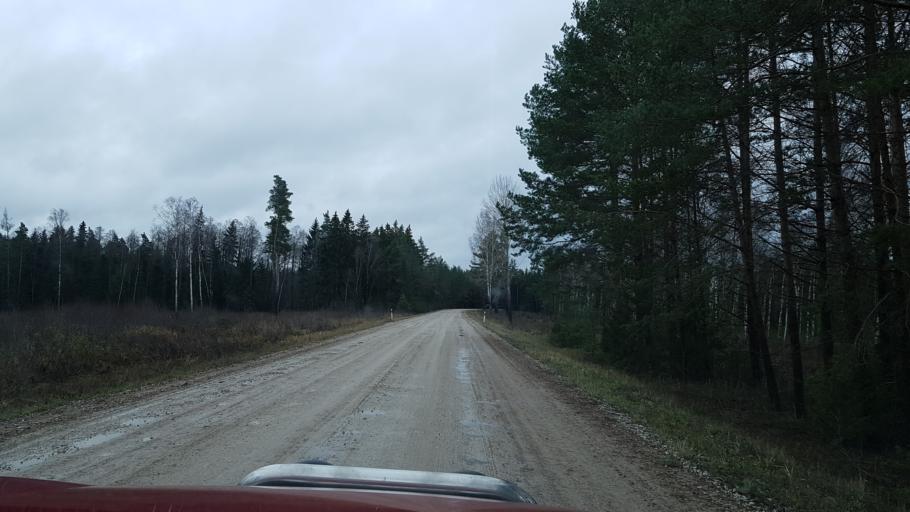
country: EE
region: Paernumaa
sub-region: Halinga vald
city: Parnu-Jaagupi
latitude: 58.5473
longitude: 24.4121
